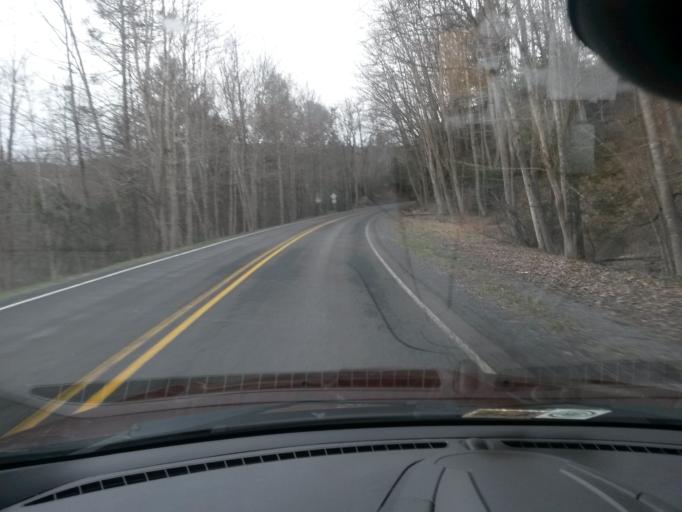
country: US
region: Virginia
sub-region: Bath County
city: Warm Springs
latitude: 38.1670
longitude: -79.7338
